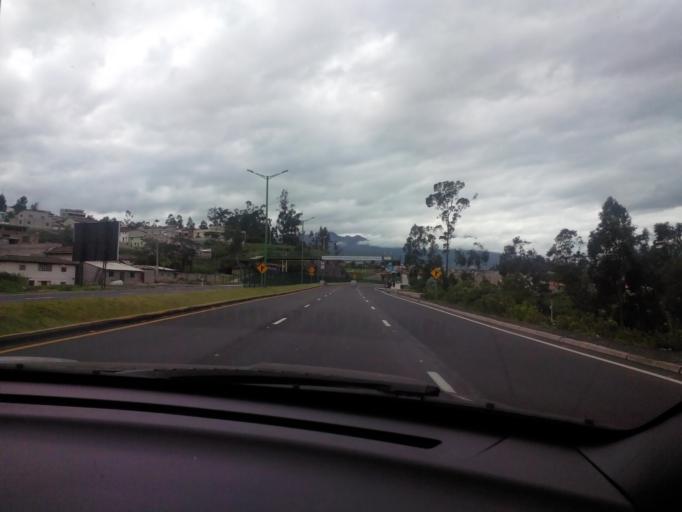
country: EC
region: Imbabura
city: Cotacachi
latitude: 0.2779
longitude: -78.2383
